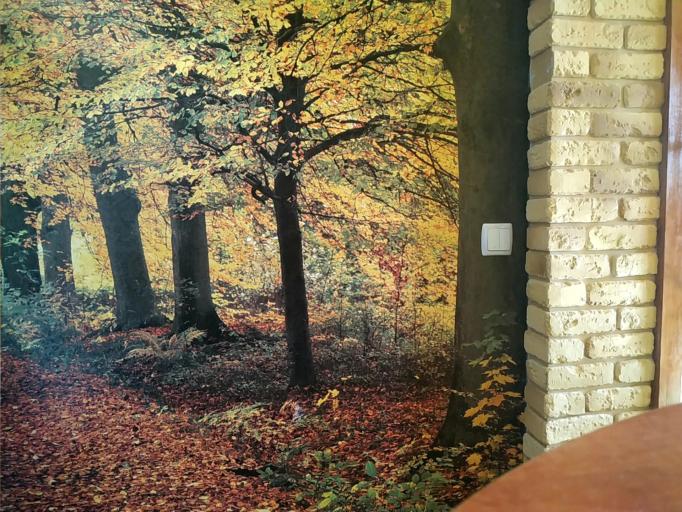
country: RU
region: Jaroslavl
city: Kukoboy
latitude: 58.8583
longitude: 39.7310
